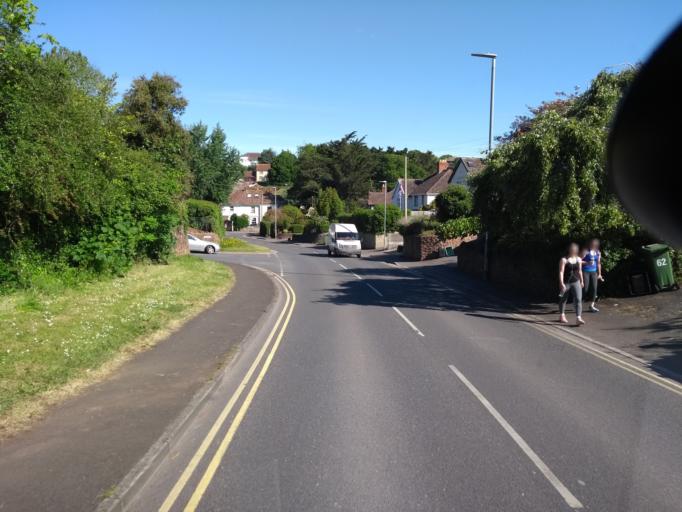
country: GB
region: England
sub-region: Somerset
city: Bridgwater
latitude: 51.1332
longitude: -3.0227
